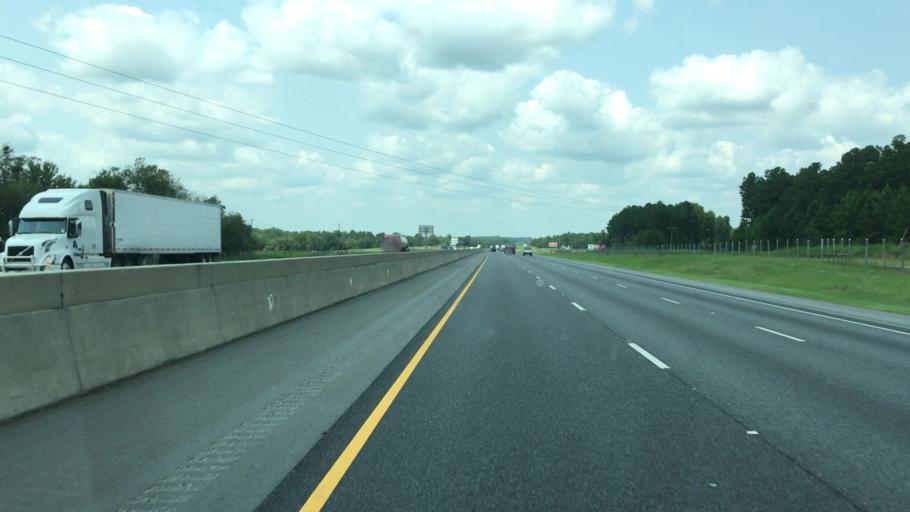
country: US
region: Georgia
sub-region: Tift County
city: Tifton
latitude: 31.5828
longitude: -83.5538
